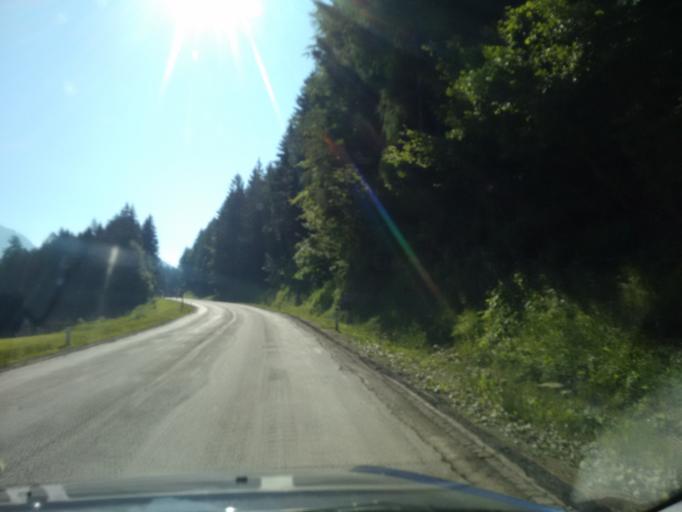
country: AT
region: Styria
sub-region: Politischer Bezirk Liezen
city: Altaussee
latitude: 47.6249
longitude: 13.7426
